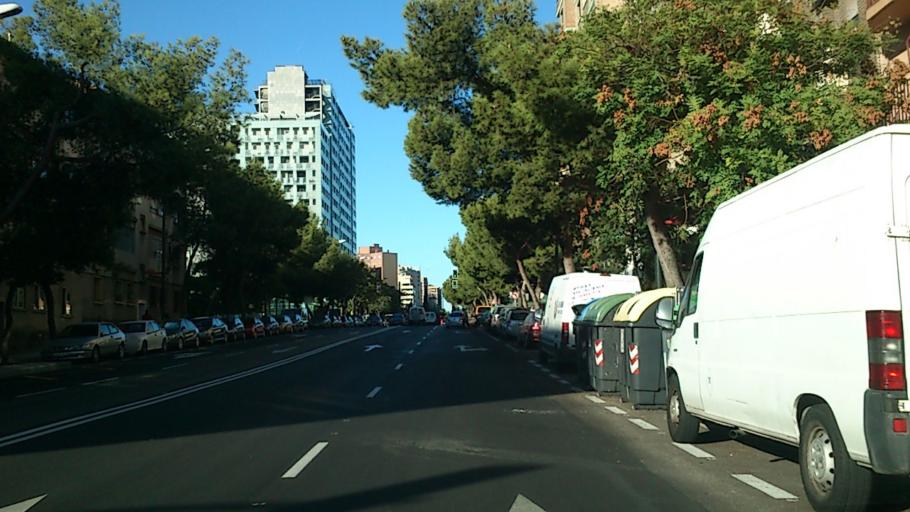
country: ES
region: Aragon
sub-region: Provincia de Zaragoza
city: Delicias
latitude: 41.6476
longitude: -0.9040
